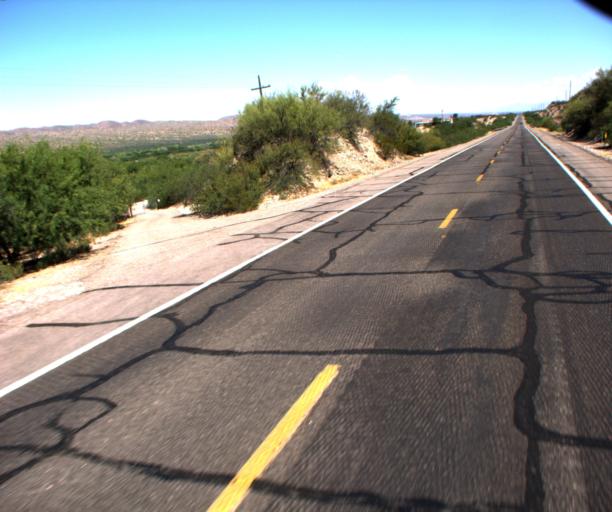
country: US
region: Arizona
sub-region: Pinal County
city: Mammoth
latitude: 32.7761
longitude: -110.6627
